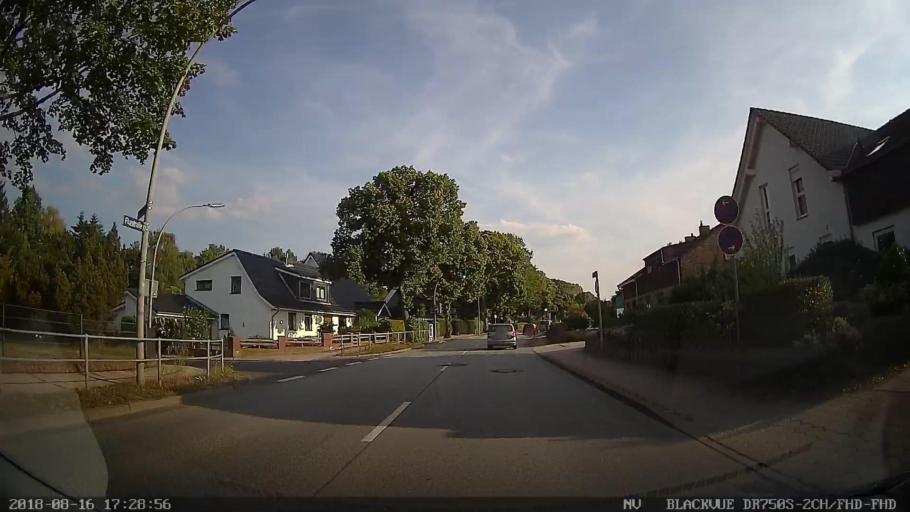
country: DE
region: Hamburg
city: Eidelstedt
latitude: 53.5816
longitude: 9.8668
